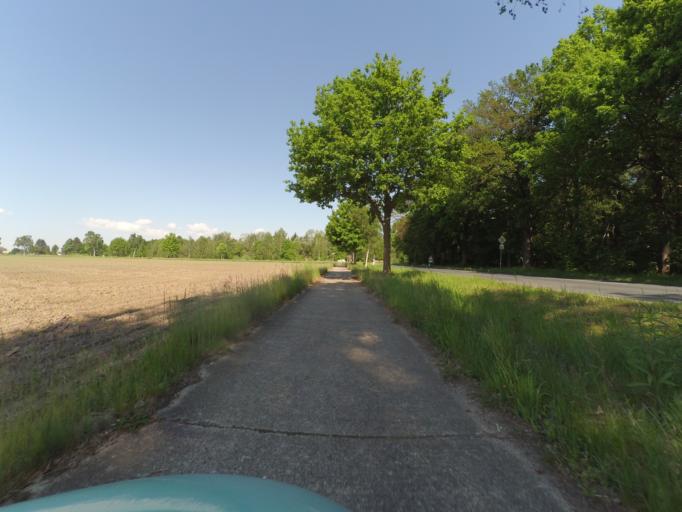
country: DE
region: Lower Saxony
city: Burgdorf
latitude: 52.4490
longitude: 9.9292
